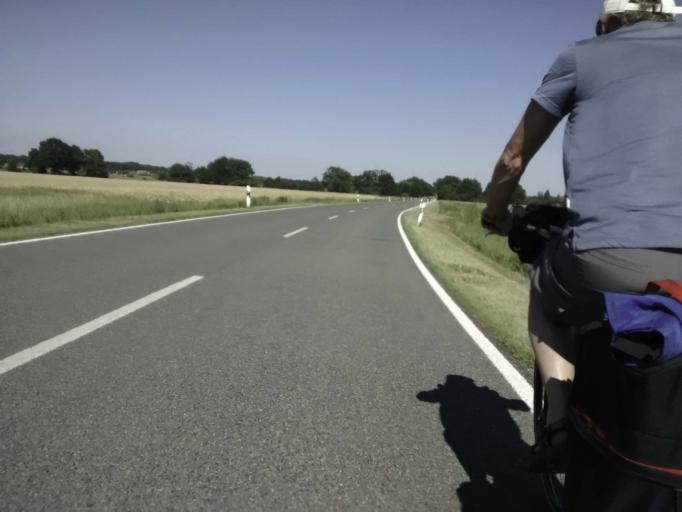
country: DE
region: Saxony-Anhalt
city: Gross Rosenburg
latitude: 51.9195
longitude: 11.9349
